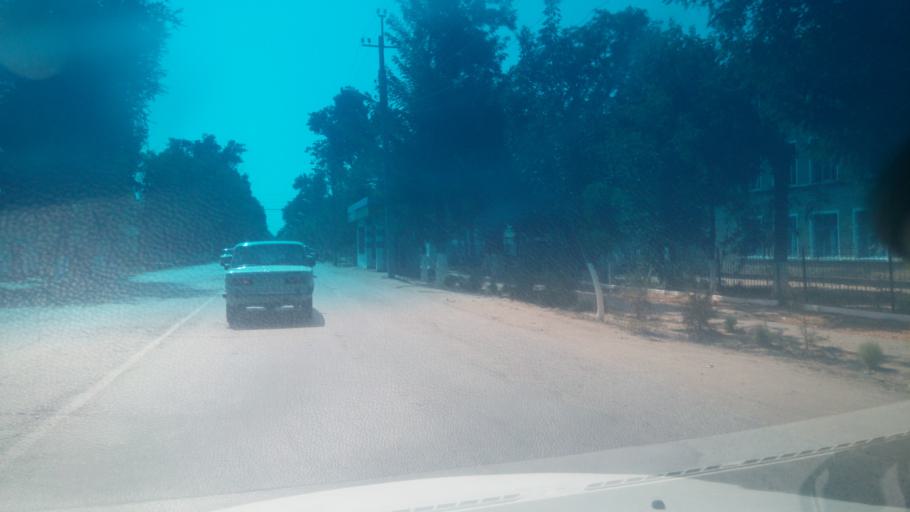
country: UZ
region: Sirdaryo
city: Sirdaryo
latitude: 40.8376
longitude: 68.6637
